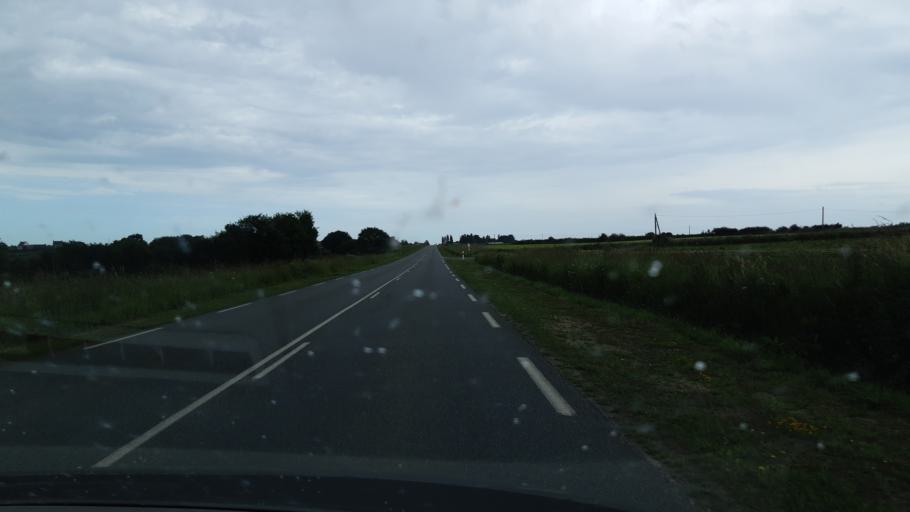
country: FR
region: Brittany
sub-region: Departement du Finistere
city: Plougoulm
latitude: 48.6344
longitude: -4.0545
